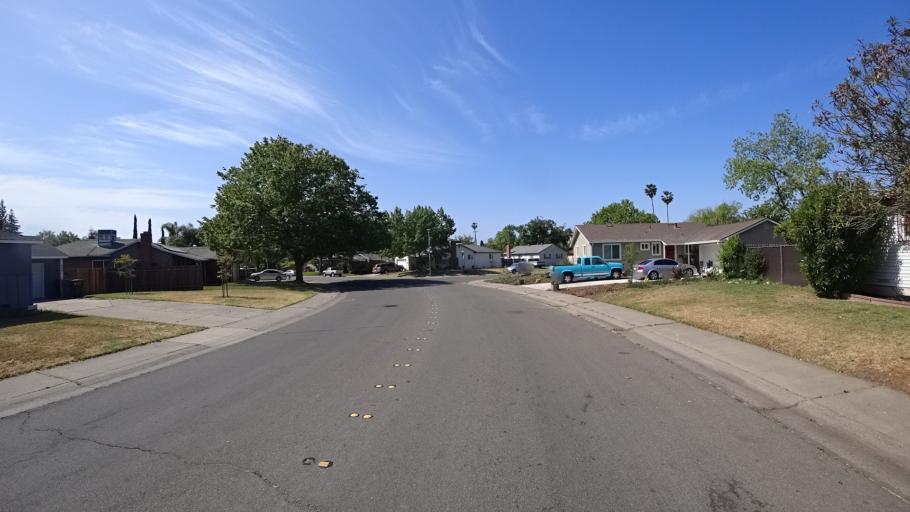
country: US
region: California
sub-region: Sacramento County
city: Parkway
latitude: 38.5101
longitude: -121.4883
